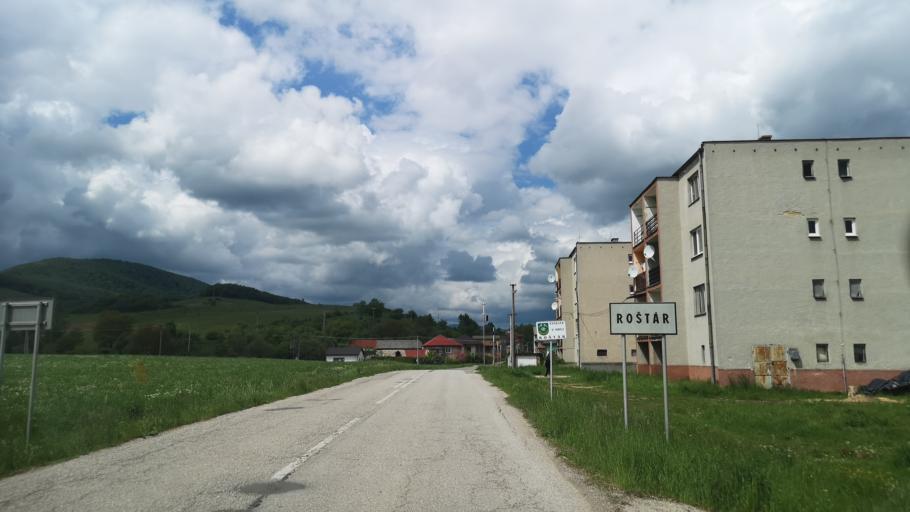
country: SK
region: Kosicky
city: Dobsina
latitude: 48.6875
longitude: 20.3479
